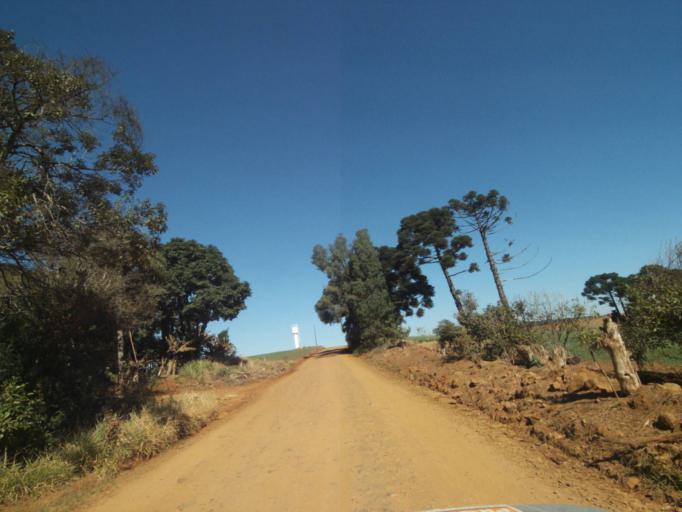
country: BR
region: Parana
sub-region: Tibagi
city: Tibagi
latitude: -24.5579
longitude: -50.6216
